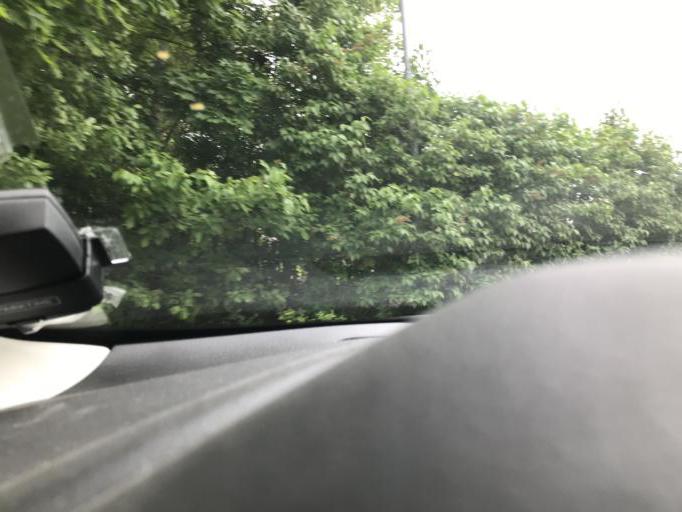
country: SE
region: Stockholm
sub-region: Botkyrka Kommun
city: Tumba
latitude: 59.1953
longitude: 17.8227
